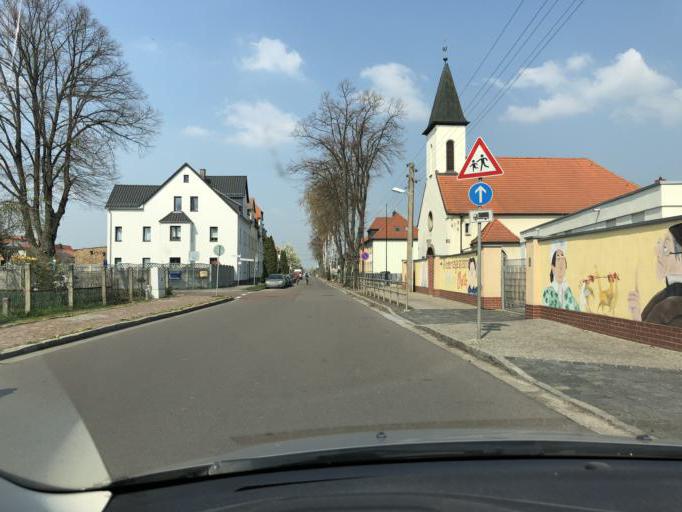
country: DE
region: Saxony-Anhalt
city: Zorbig
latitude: 51.6308
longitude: 12.1223
